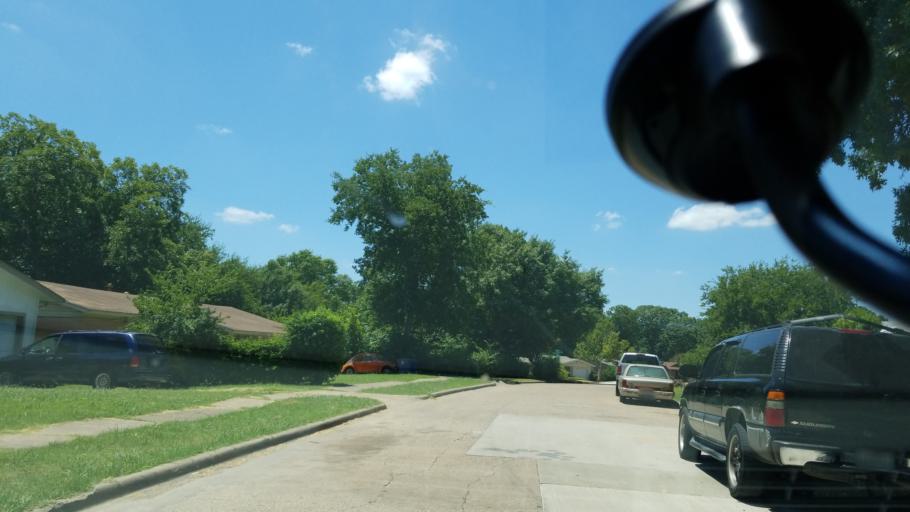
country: US
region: Texas
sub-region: Dallas County
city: Cockrell Hill
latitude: 32.6919
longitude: -96.8161
